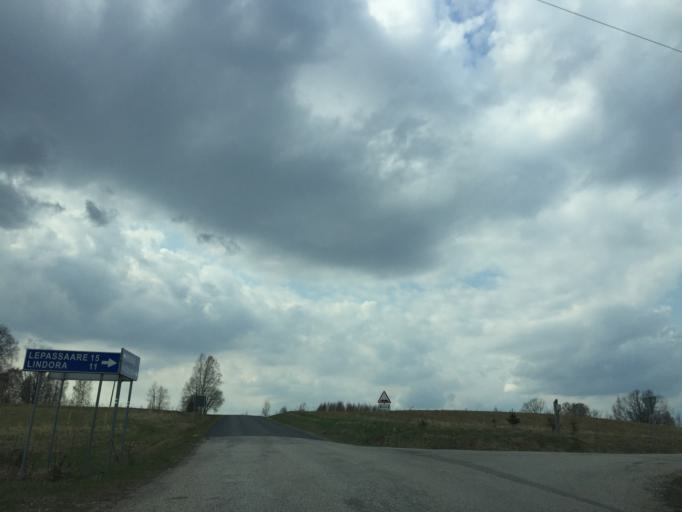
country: RU
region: Pskov
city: Pechory
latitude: 57.7323
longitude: 27.3485
